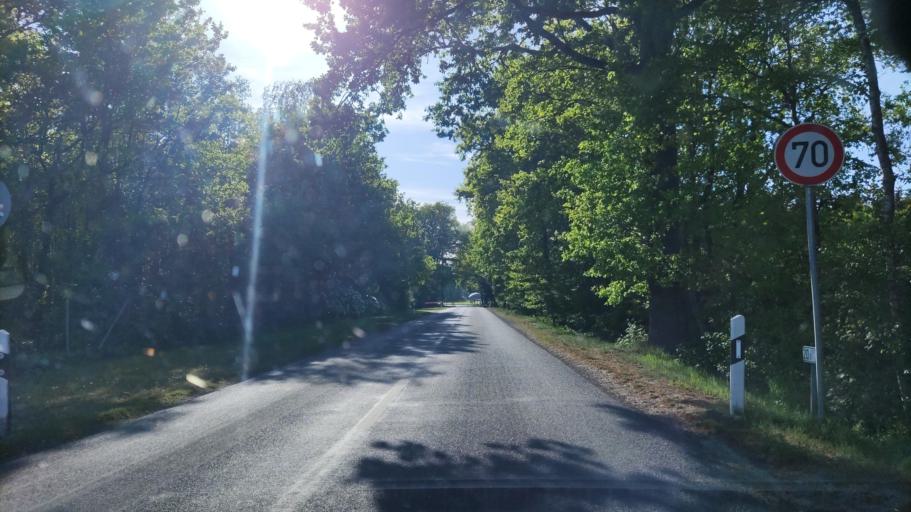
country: DE
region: Lower Saxony
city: Schneverdingen
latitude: 53.1771
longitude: 9.7964
